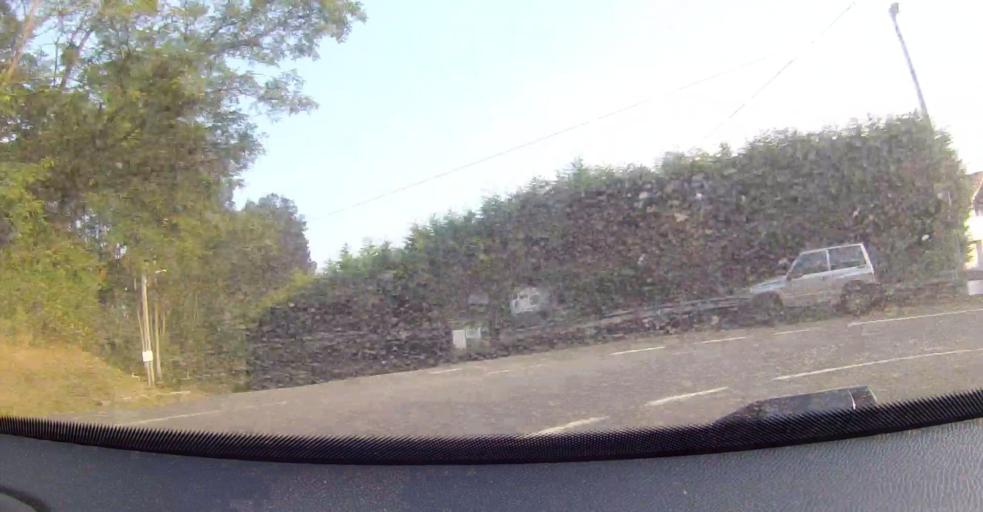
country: ES
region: Basque Country
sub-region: Bizkaia
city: Sopuerta
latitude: 43.2884
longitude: -3.1593
